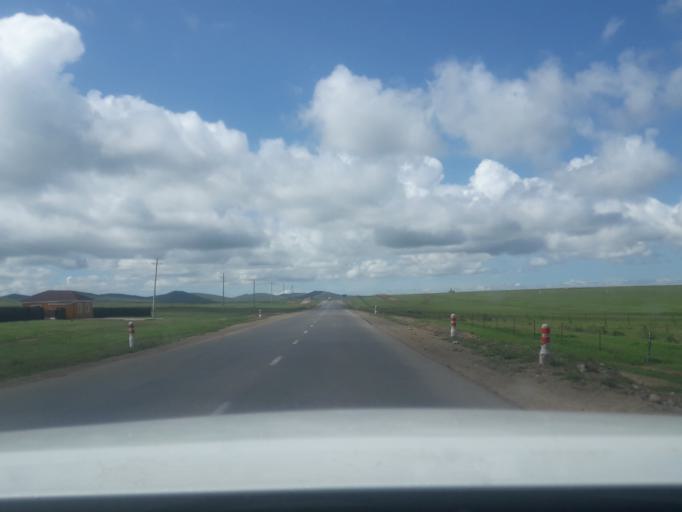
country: MN
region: Central Aimak
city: Altanbulag
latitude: 47.9011
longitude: 106.4868
